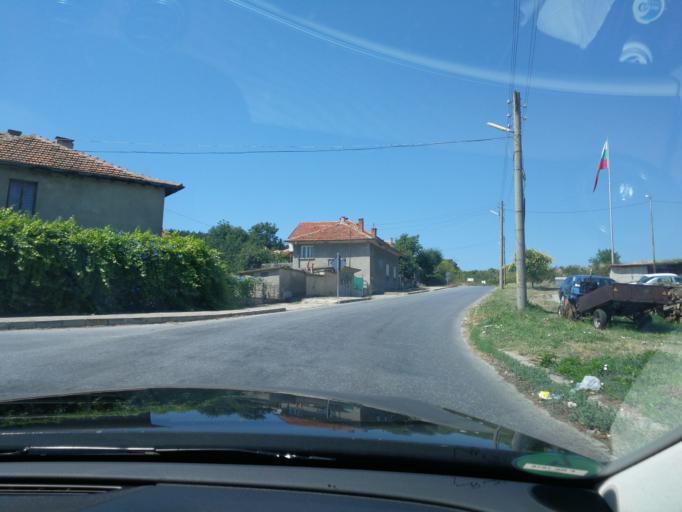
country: BG
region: Khaskovo
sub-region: Obshtina Topolovgrad
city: Topolovgrad
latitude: 42.0828
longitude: 26.3281
